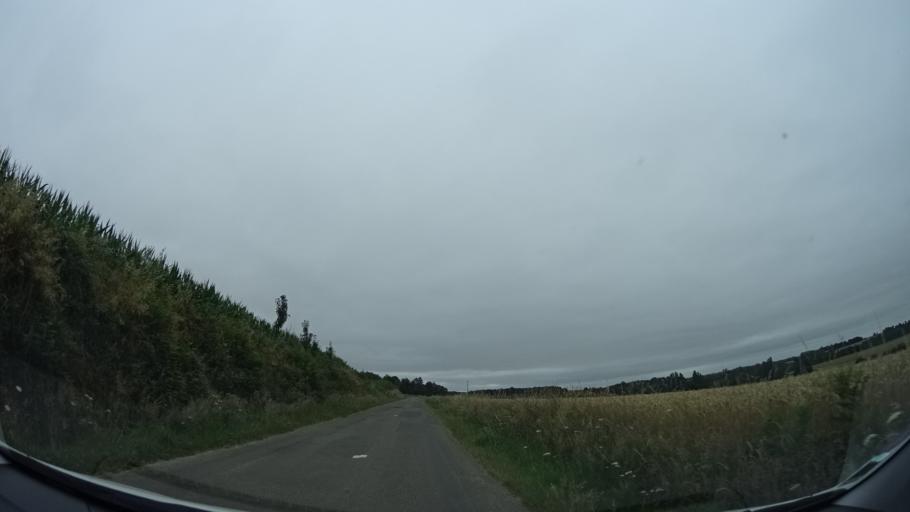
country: FR
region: Brittany
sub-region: Departement des Cotes-d'Armor
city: Evran
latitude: 48.3229
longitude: -1.9325
